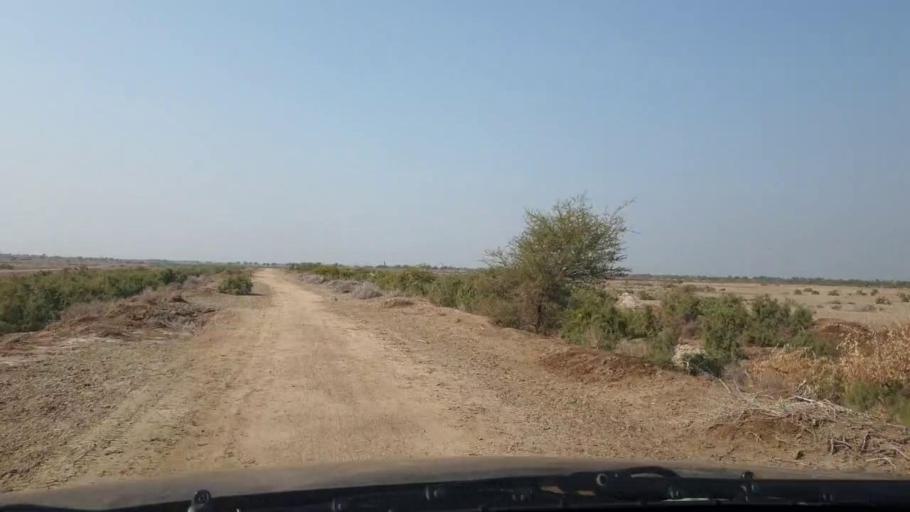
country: PK
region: Sindh
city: Jhol
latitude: 25.8917
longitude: 68.9665
